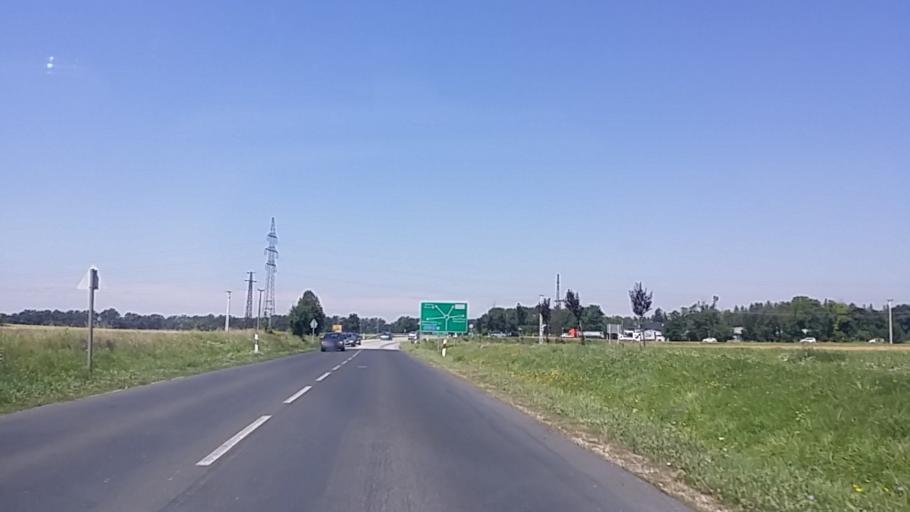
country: HU
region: Zala
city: Keszthely
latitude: 46.7765
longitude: 17.2295
